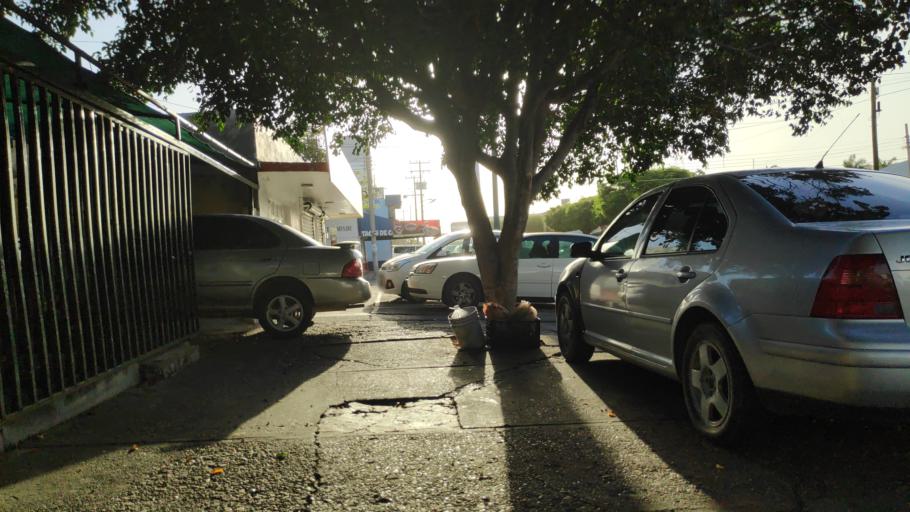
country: MX
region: Sinaloa
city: Culiacan
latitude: 24.8009
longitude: -107.3963
